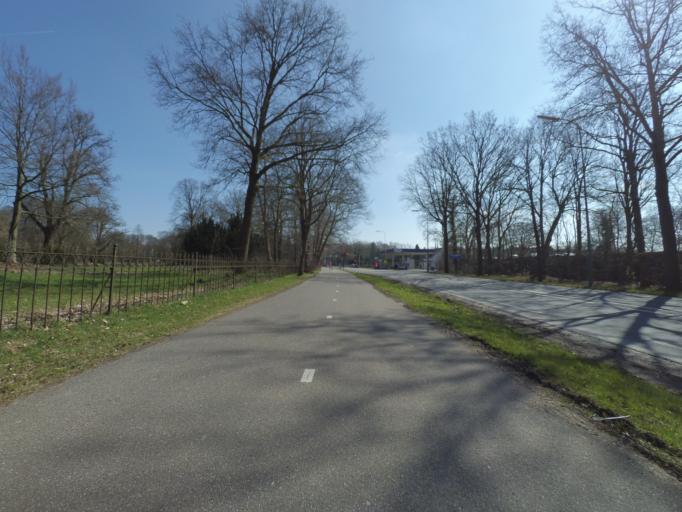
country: NL
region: Utrecht
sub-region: Gemeente Utrechtse Heuvelrug
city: Driebergen-Rijsenburg
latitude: 52.0437
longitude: 5.3021
